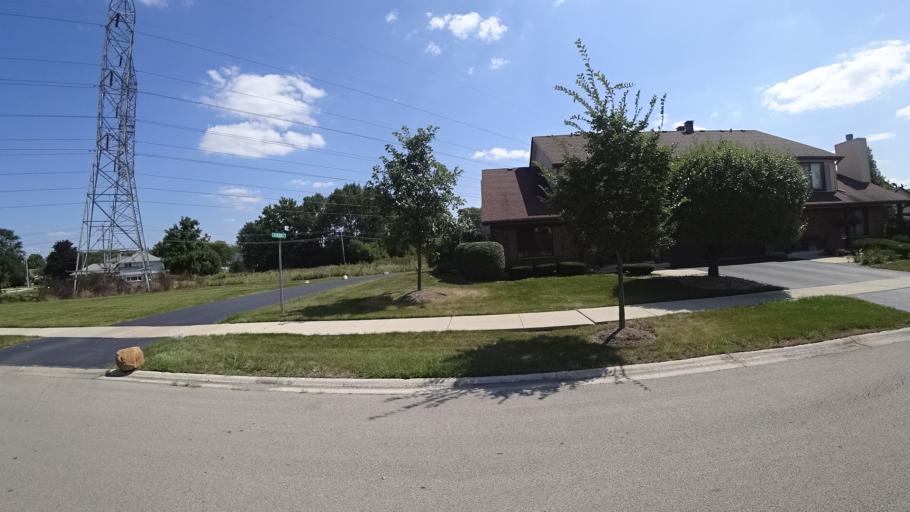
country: US
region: Illinois
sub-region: Cook County
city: Orland Park
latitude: 41.6385
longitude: -87.8470
